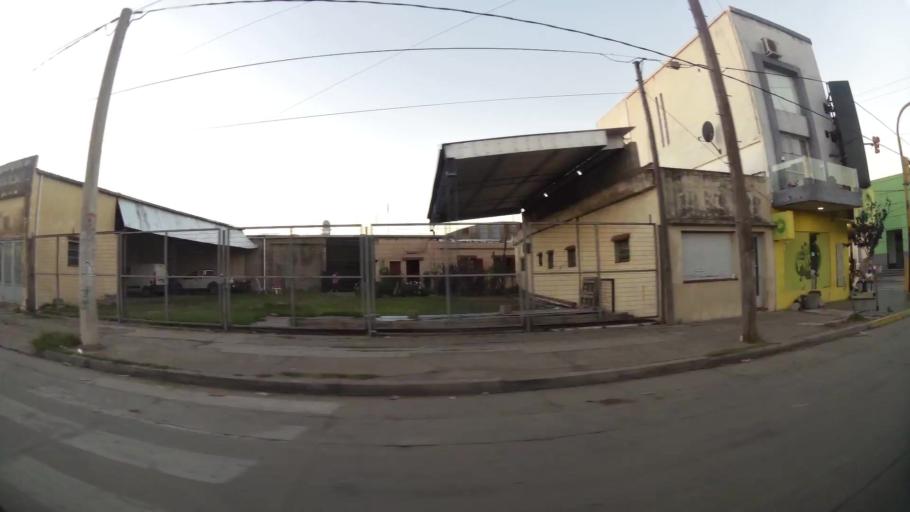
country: AR
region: Cordoba
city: Villa Maria
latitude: -32.4091
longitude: -63.2569
